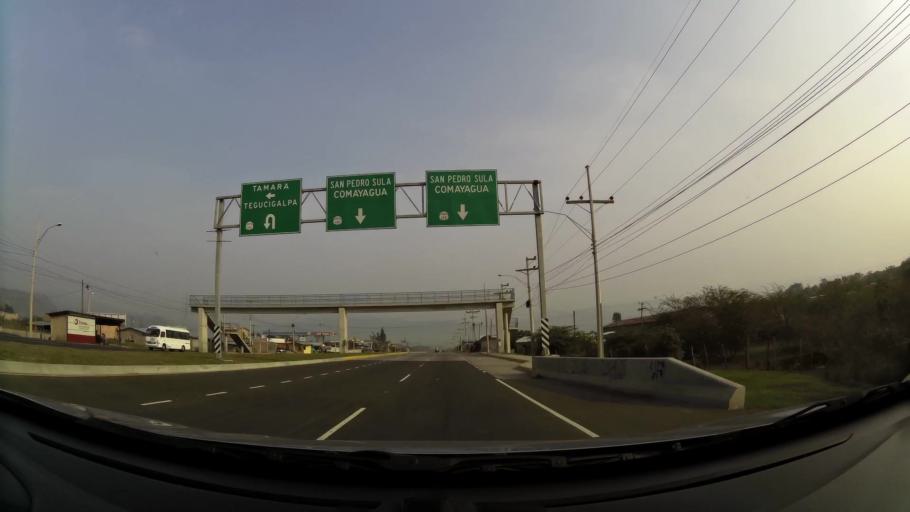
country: HN
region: Francisco Morazan
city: Tamara
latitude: 14.2013
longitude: -87.3457
